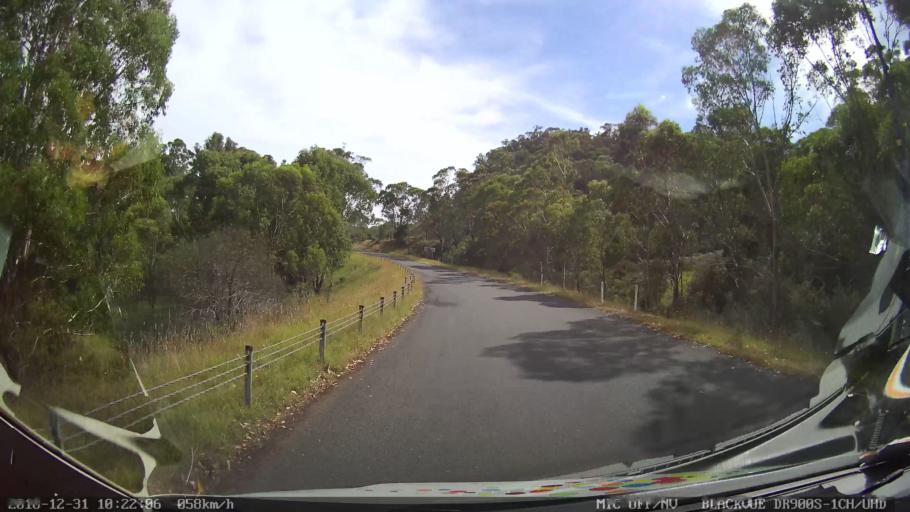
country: AU
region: New South Wales
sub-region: Snowy River
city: Jindabyne
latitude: -36.5285
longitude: 148.1427
